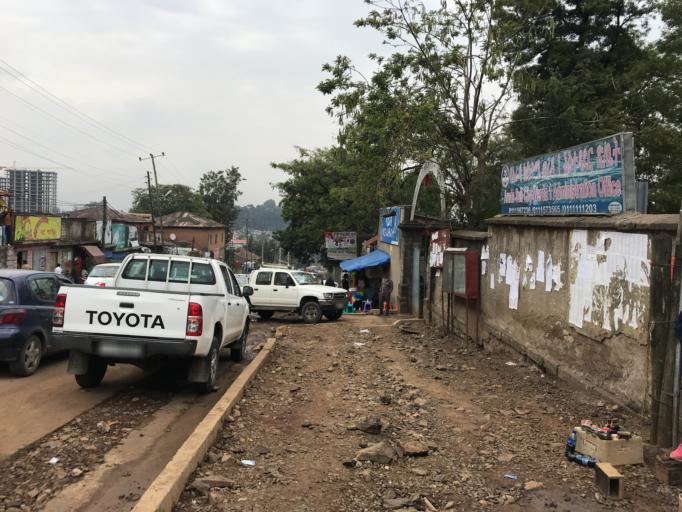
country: ET
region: Adis Abeba
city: Addis Ababa
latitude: 9.0310
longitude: 38.7556
